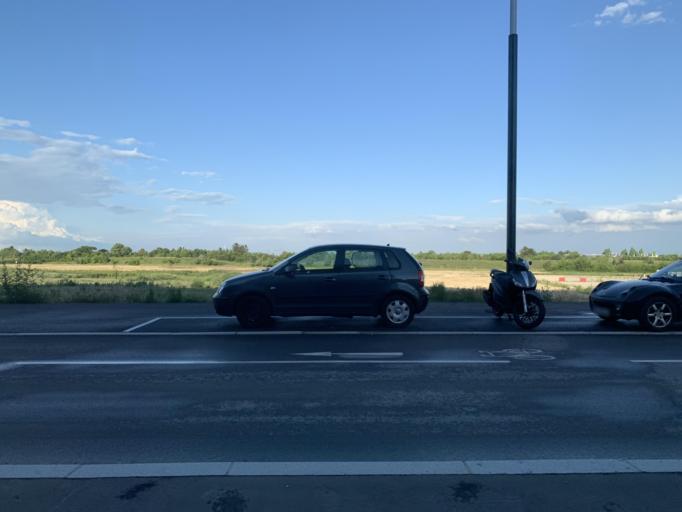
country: AT
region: Lower Austria
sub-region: Politischer Bezirk Ganserndorf
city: Gross-Enzersdorf
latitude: 48.2300
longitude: 16.5126
